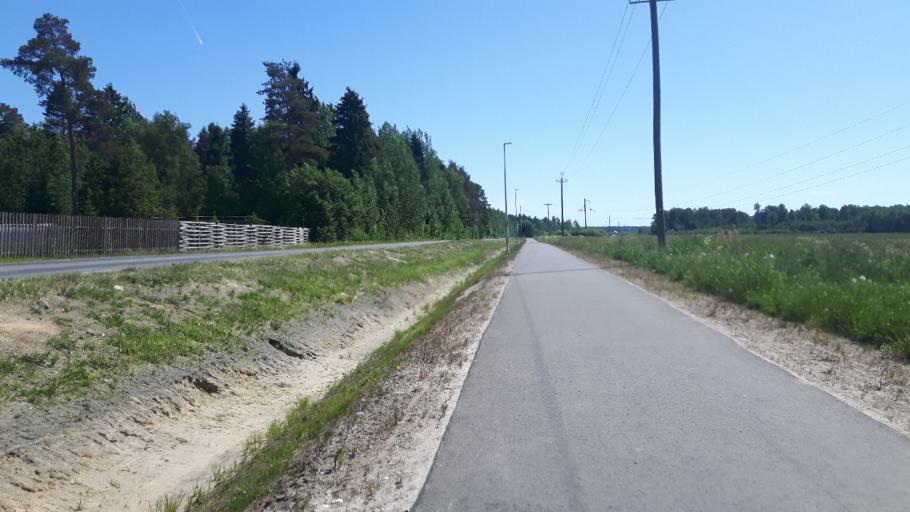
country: EE
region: Raplamaa
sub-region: Kohila vald
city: Kohila
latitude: 59.2121
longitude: 24.6813
